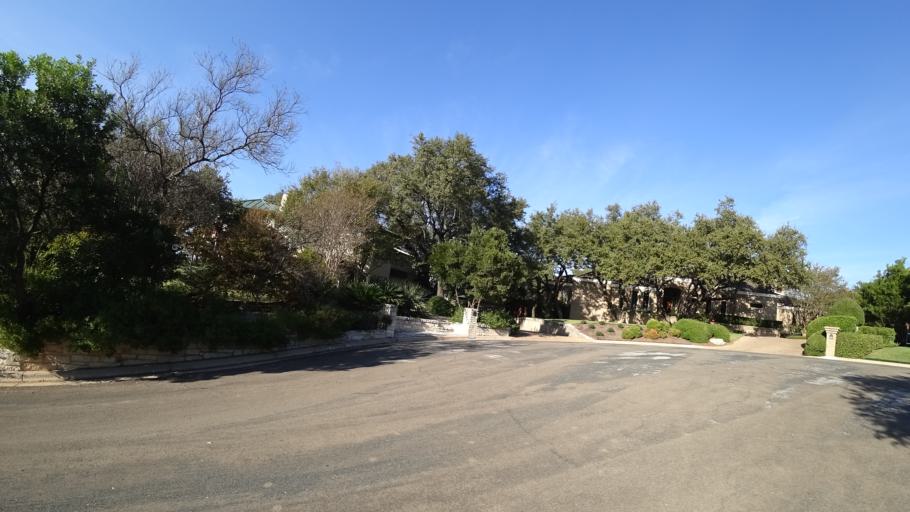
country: US
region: Texas
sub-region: Williamson County
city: Anderson Mill
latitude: 30.4362
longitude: -97.8104
